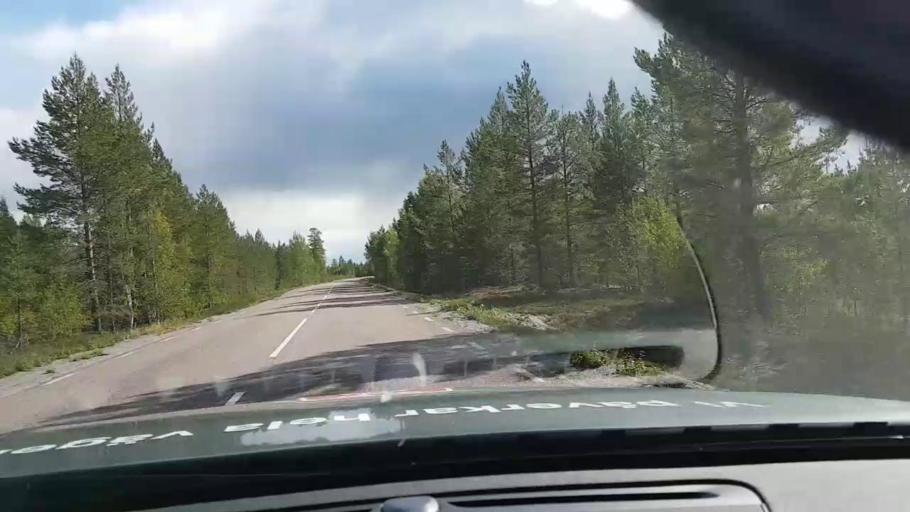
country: SE
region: Vaesterbotten
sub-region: Asele Kommun
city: Asele
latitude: 63.9064
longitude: 17.3425
